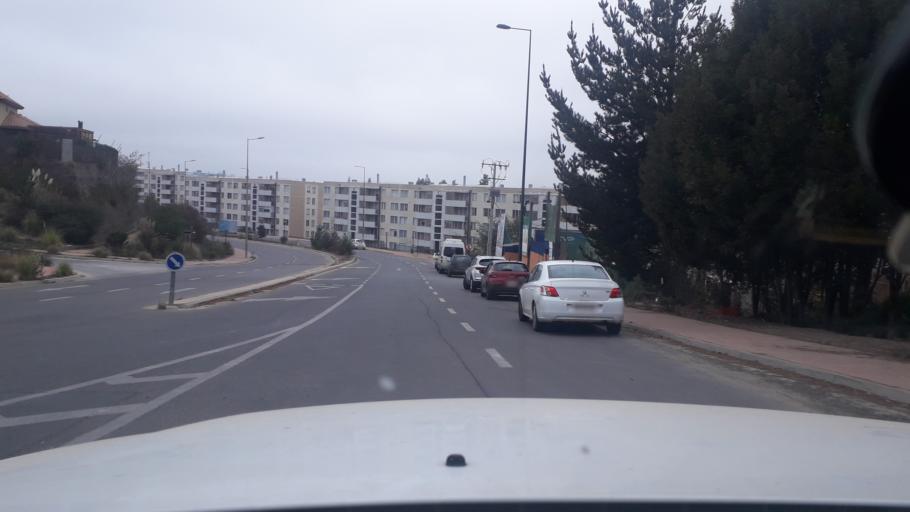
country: CL
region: Valparaiso
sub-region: Provincia de Valparaiso
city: Valparaiso
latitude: -33.1353
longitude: -71.5735
